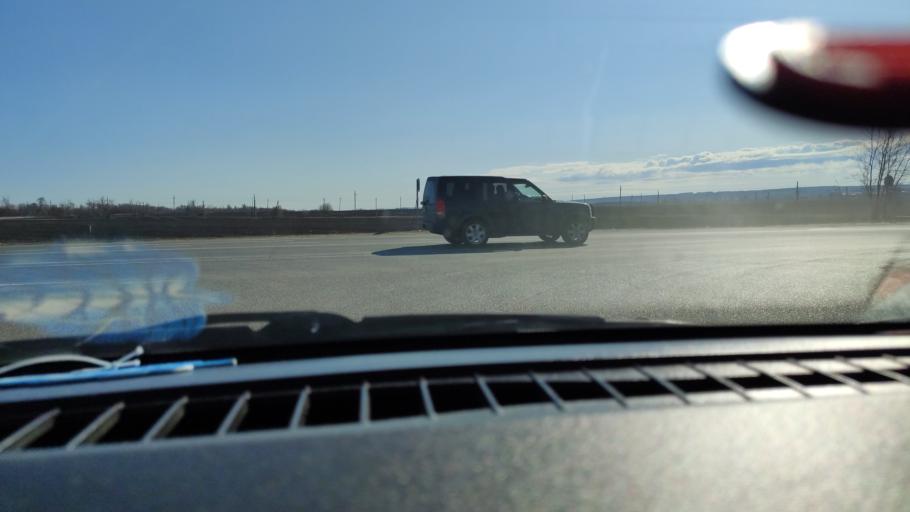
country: RU
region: Samara
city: Syzran'
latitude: 53.2043
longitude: 48.5098
